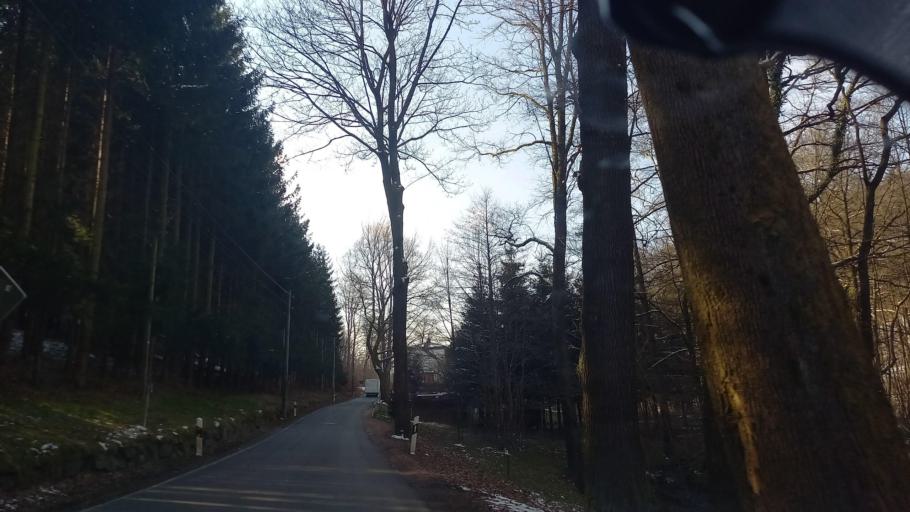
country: DE
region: Saxony
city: Kirchberg
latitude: 50.5831
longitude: 12.4921
